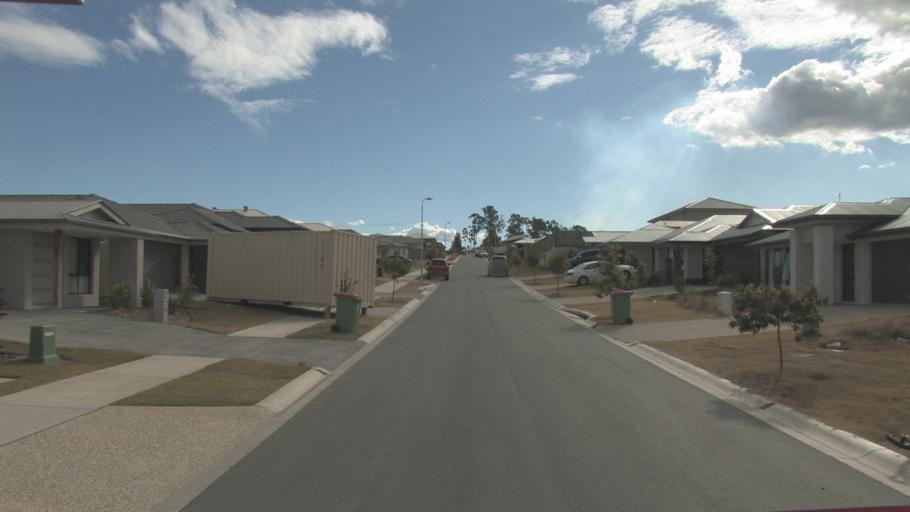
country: AU
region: Queensland
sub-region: Logan
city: Chambers Flat
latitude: -27.8056
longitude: 153.1187
